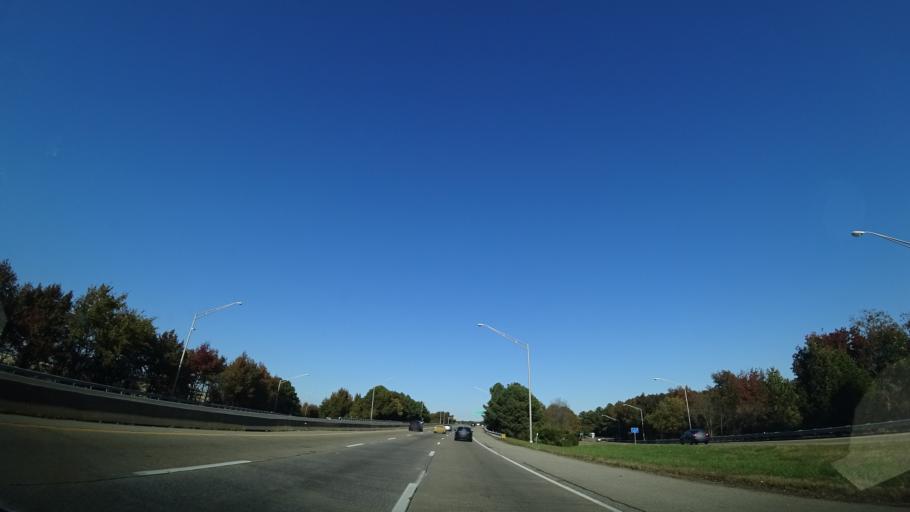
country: US
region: Virginia
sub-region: City of Newport News
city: Newport News
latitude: 37.0018
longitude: -76.4051
